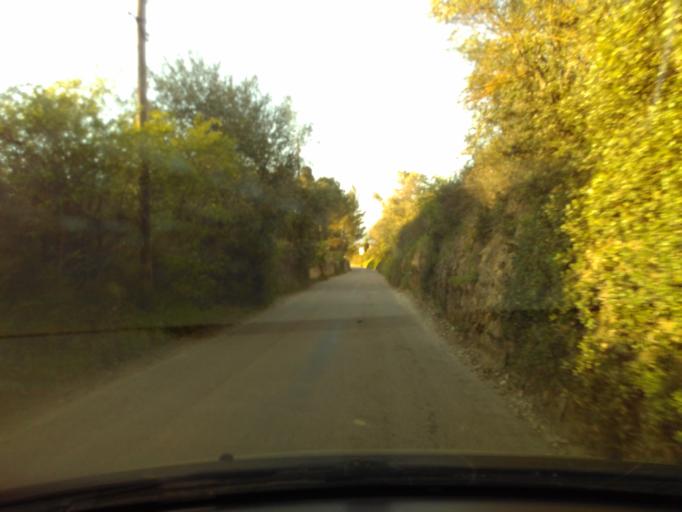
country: FR
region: Provence-Alpes-Cote d'Azur
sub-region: Departement du Vaucluse
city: Carpentras
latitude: 44.0553
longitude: 5.0703
